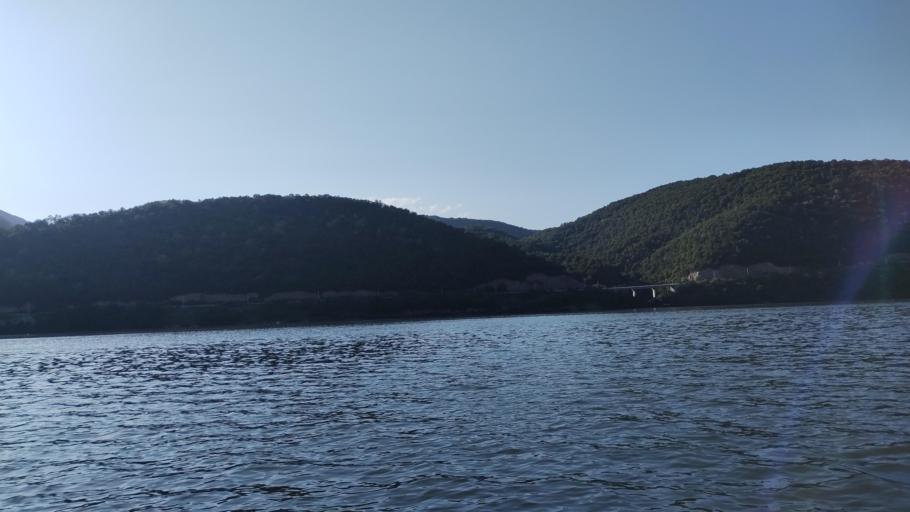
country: RO
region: Mehedinti
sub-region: Comuna Dubova
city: Dubova
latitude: 44.5806
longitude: 22.2489
